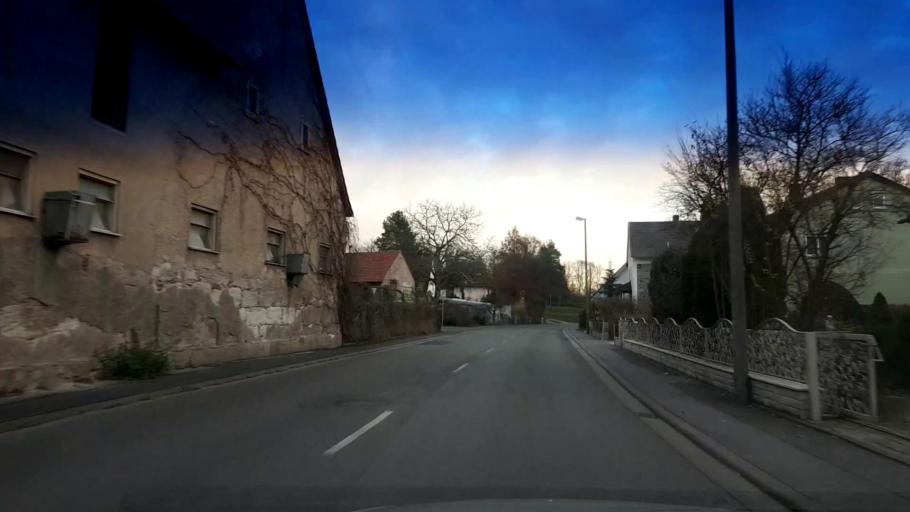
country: DE
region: Bavaria
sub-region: Upper Franconia
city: Walsdorf
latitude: 49.8814
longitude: 10.7609
